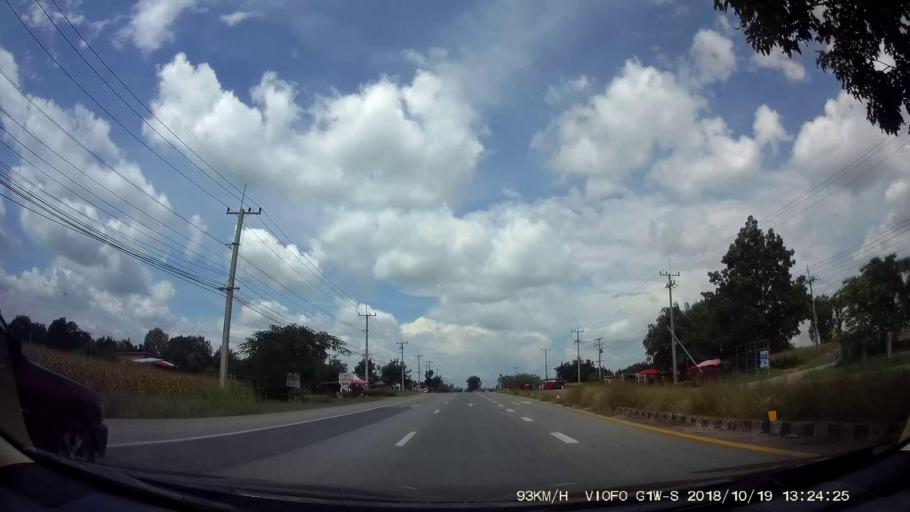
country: TH
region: Chaiyaphum
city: Chatturat
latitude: 15.5068
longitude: 101.8211
